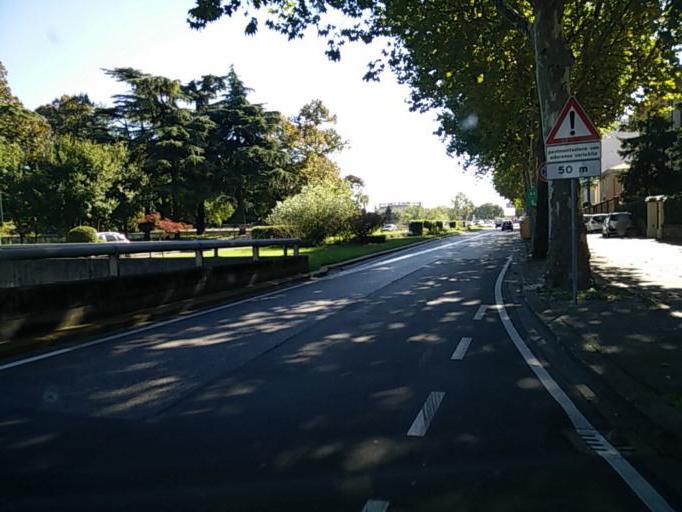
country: IT
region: Veneto
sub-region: Provincia di Verona
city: Verona
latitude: 45.4347
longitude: 10.9792
